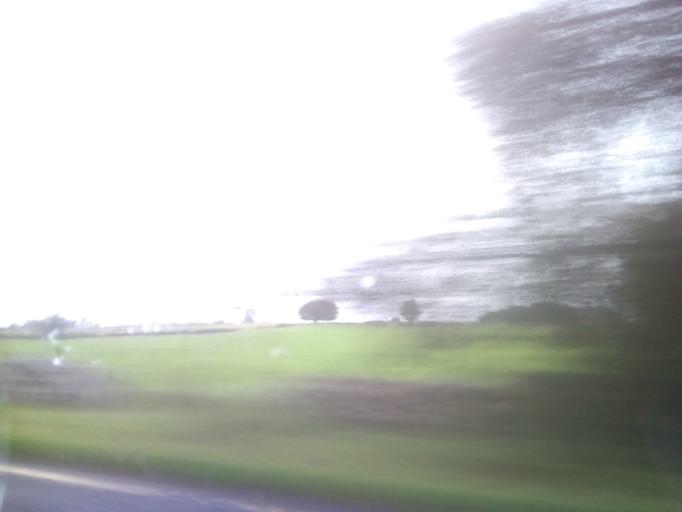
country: IE
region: Connaught
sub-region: Roscommon
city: Boyle
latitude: 53.8090
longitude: -8.3092
